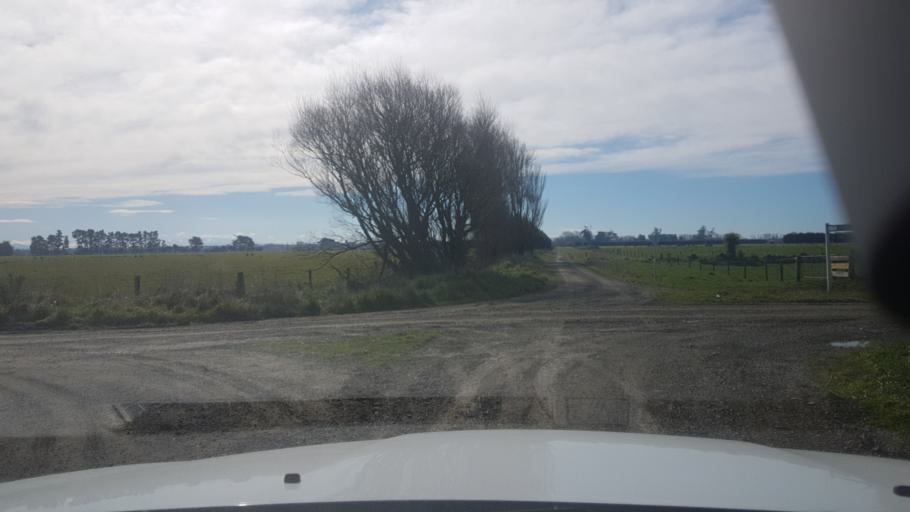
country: NZ
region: Canterbury
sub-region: Timaru District
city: Timaru
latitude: -44.2540
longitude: 171.3775
